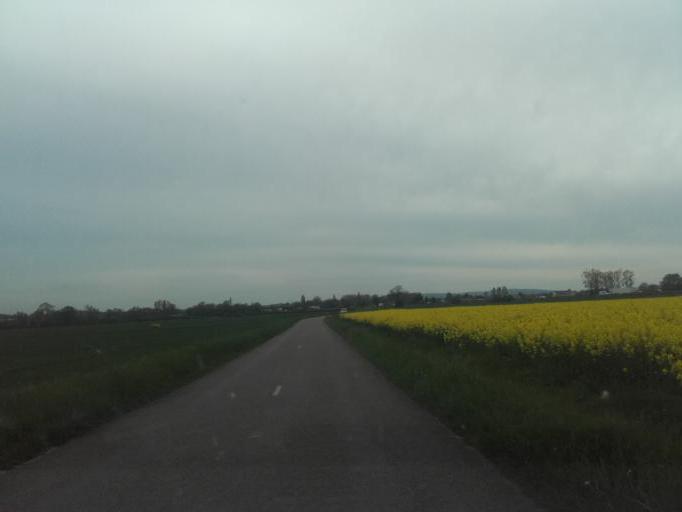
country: FR
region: Bourgogne
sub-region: Departement de Saone-et-Loire
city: Demigny
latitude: 46.9468
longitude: 4.8328
